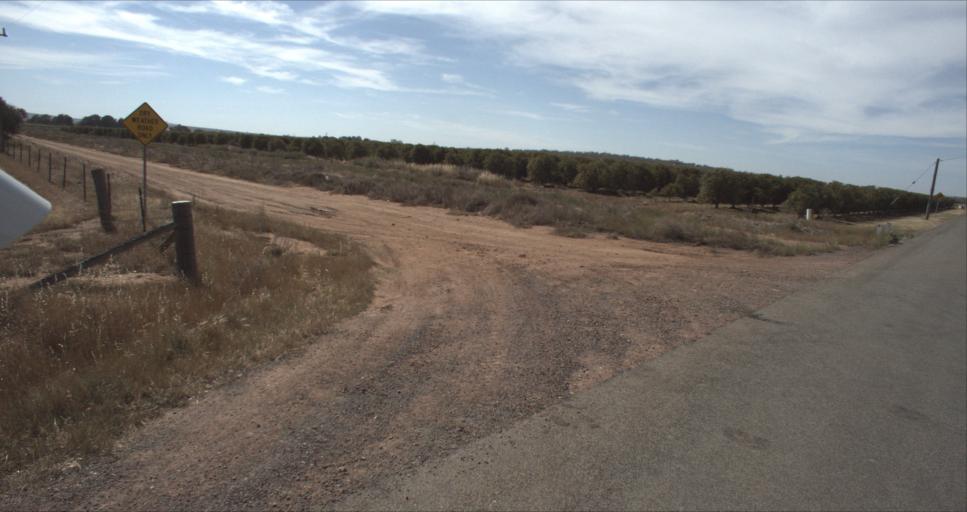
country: AU
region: New South Wales
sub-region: Leeton
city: Leeton
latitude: -34.5731
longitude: 146.4668
